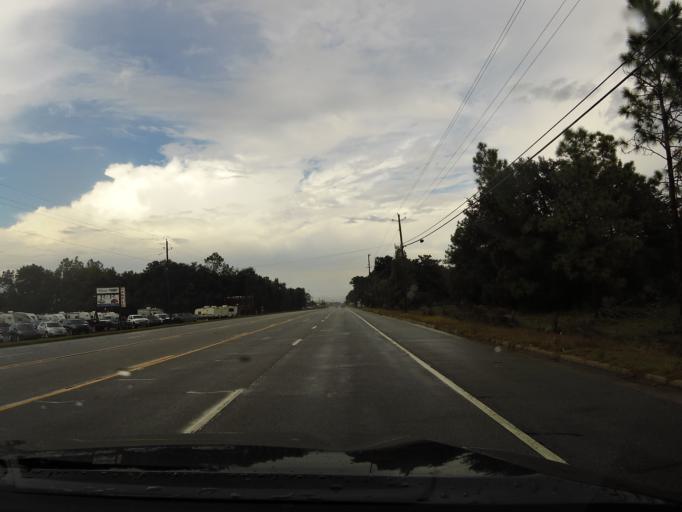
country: US
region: Georgia
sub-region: Wayne County
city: Jesup
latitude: 31.6394
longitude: -81.8599
